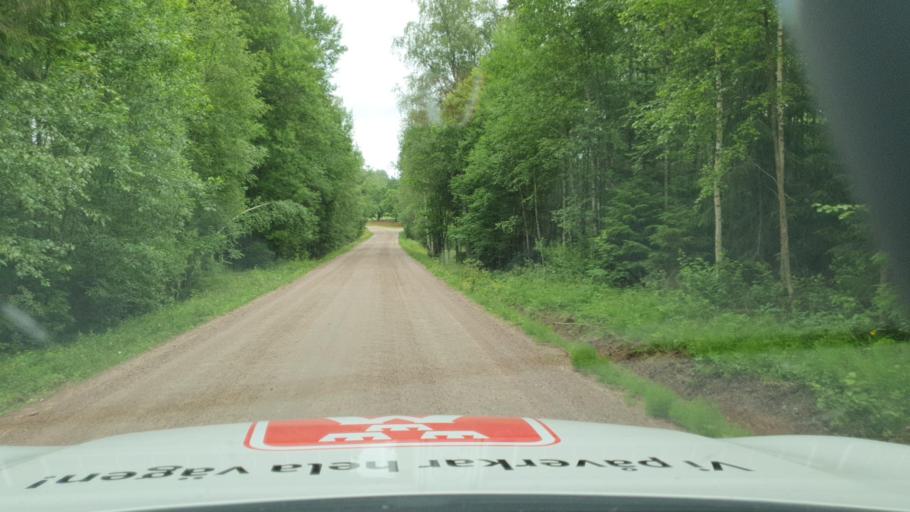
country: SE
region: Vaermland
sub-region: Kristinehamns Kommun
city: Kristinehamn
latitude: 59.5283
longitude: 13.9643
